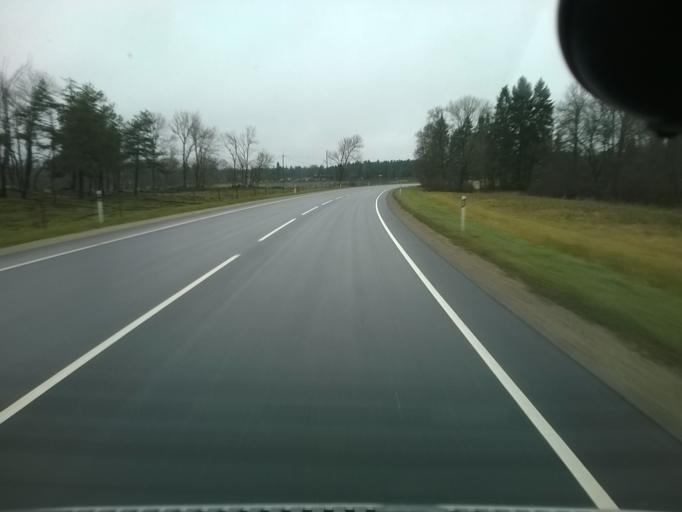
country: EE
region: Harju
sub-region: Nissi vald
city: Turba
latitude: 59.0256
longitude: 24.1495
